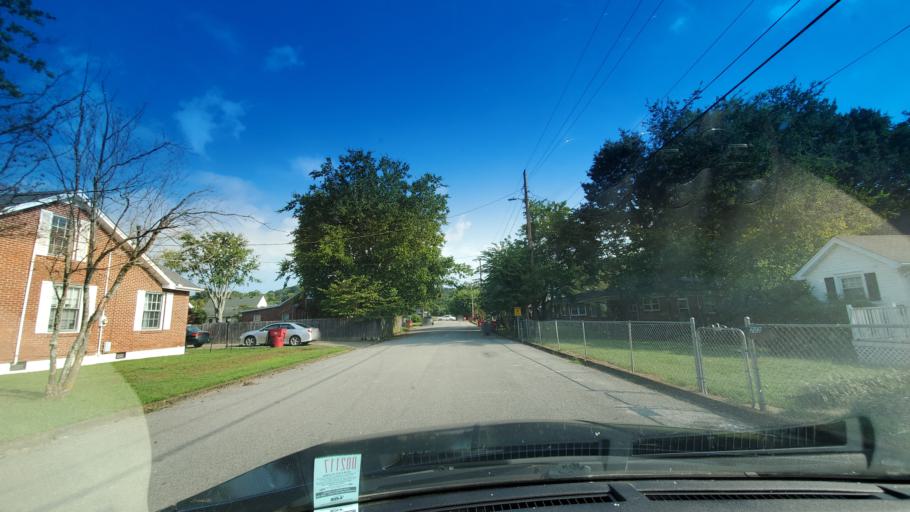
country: US
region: Tennessee
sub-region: Smith County
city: Carthage
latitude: 36.2566
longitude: -85.9455
